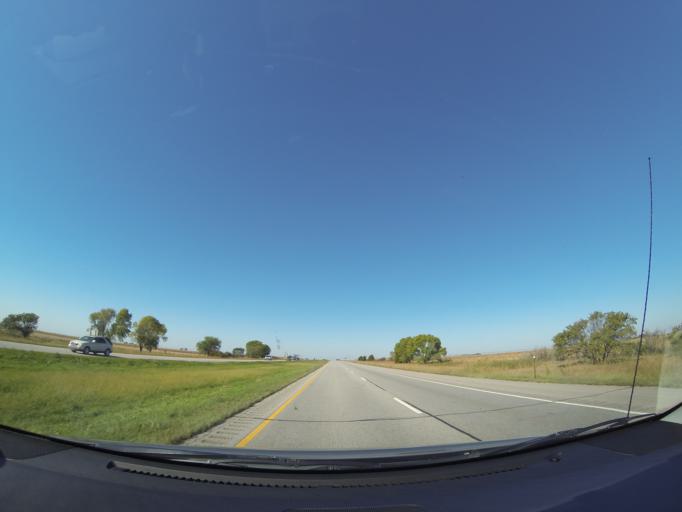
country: US
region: Nebraska
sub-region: Seward County
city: Milford
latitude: 40.8224
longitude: -97.1219
